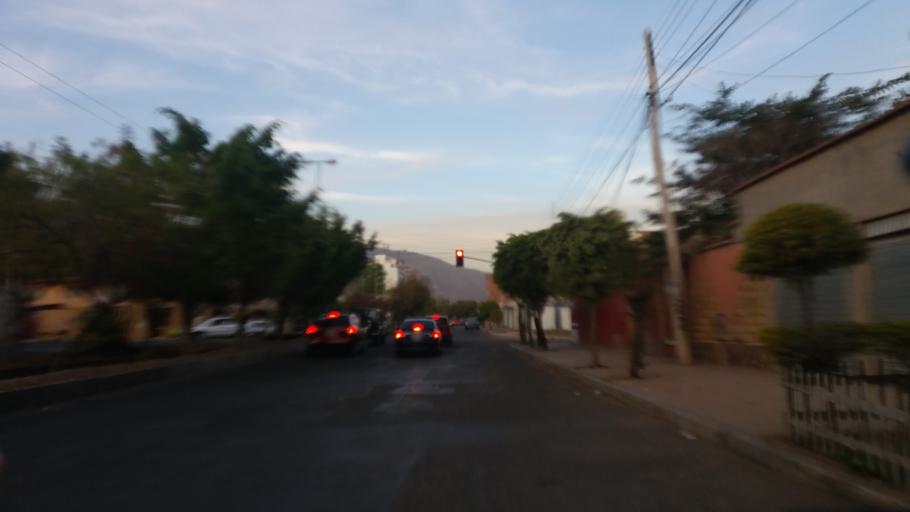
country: BO
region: Cochabamba
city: Cochabamba
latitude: -17.3831
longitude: -66.1799
